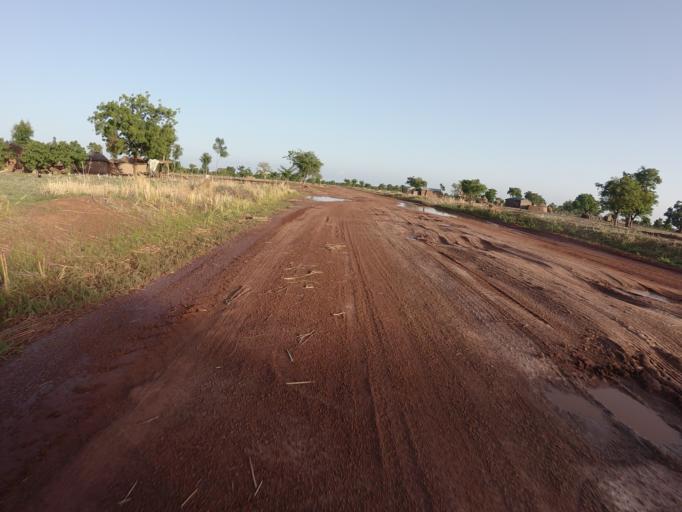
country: TG
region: Savanes
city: Sansanne-Mango
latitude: 10.2958
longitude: -0.0884
